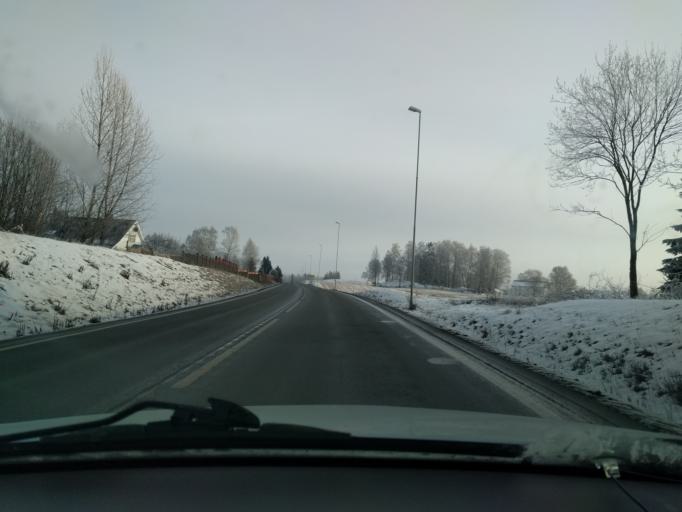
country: NO
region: Hedmark
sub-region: Stange
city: Stange
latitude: 60.8151
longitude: 11.1806
